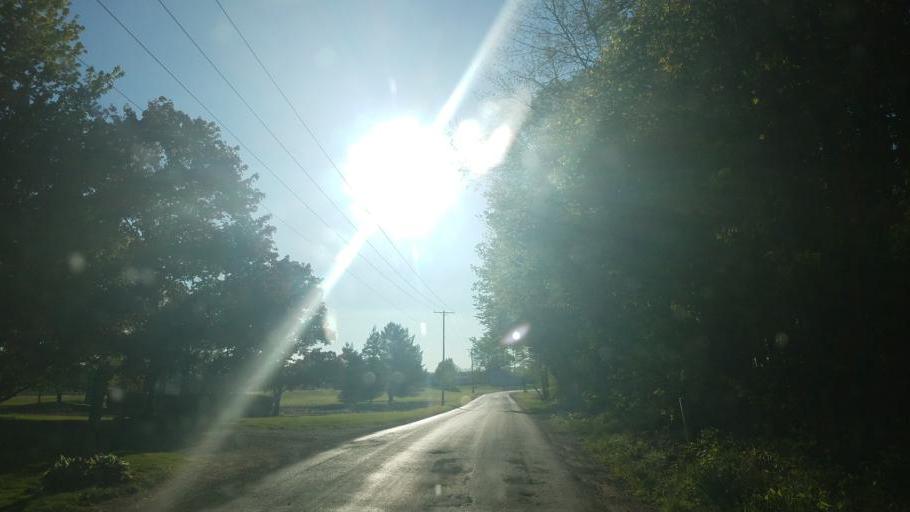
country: US
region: Ohio
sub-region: Richland County
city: Lexington
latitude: 40.5869
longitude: -82.6490
